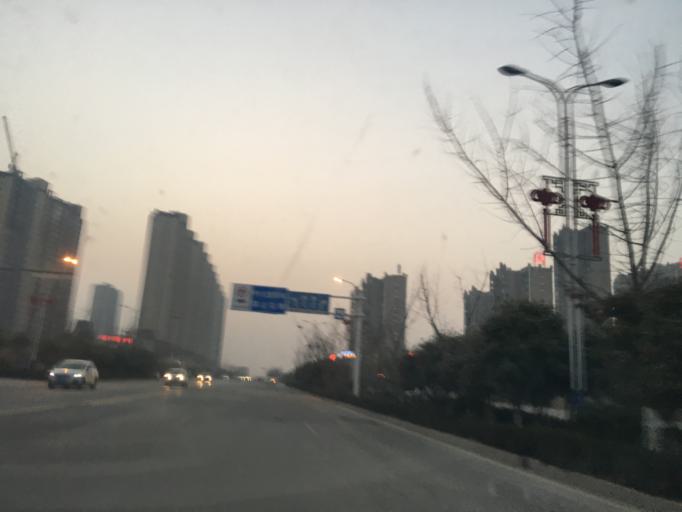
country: CN
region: Hubei
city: Nanhu
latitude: 31.1609
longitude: 115.0148
